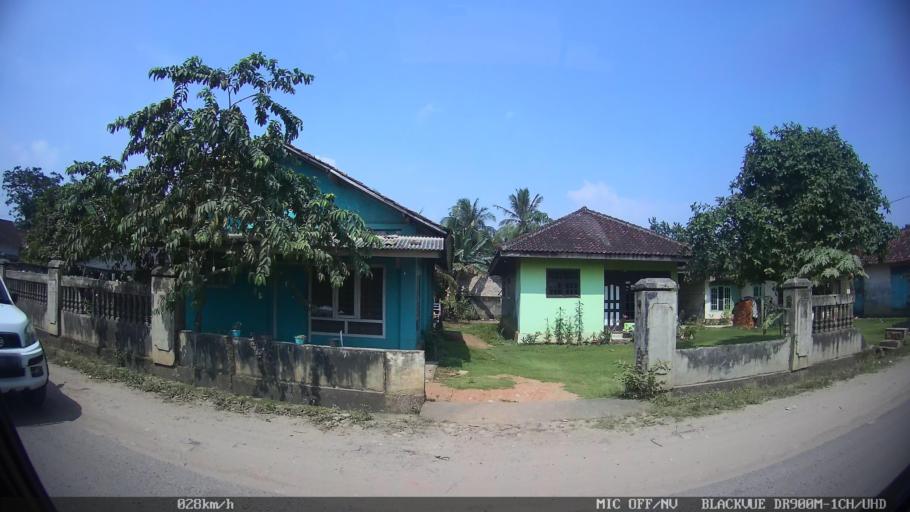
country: ID
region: Lampung
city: Natar
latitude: -5.3075
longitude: 105.2143
